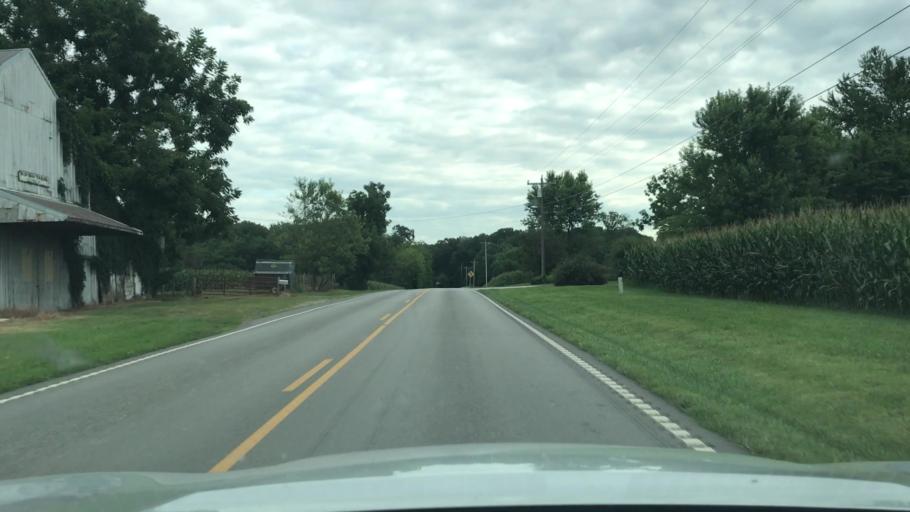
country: US
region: Kentucky
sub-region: Todd County
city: Guthrie
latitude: 36.7215
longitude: -87.1904
